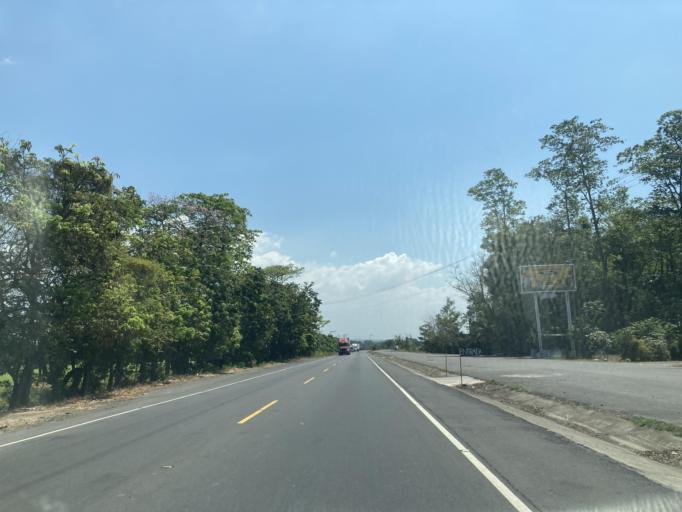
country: GT
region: Escuintla
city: Guanagazapa
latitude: 14.1054
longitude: -90.6239
